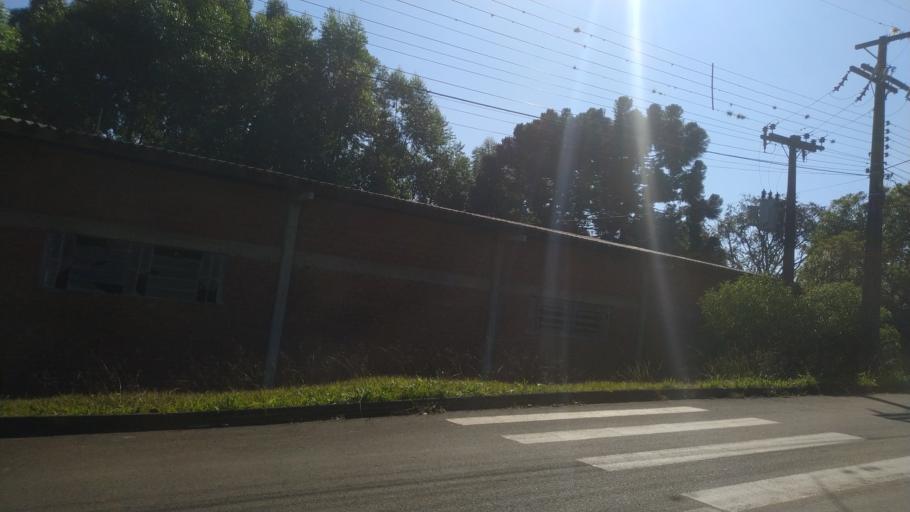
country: BR
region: Santa Catarina
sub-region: Chapeco
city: Chapeco
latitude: -27.0772
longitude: -52.6057
